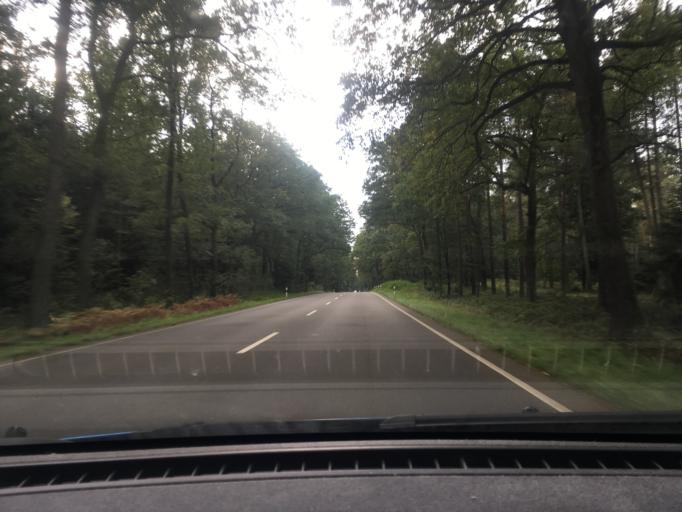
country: DE
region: Lower Saxony
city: Sprakensehl
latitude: 52.8218
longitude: 10.4560
